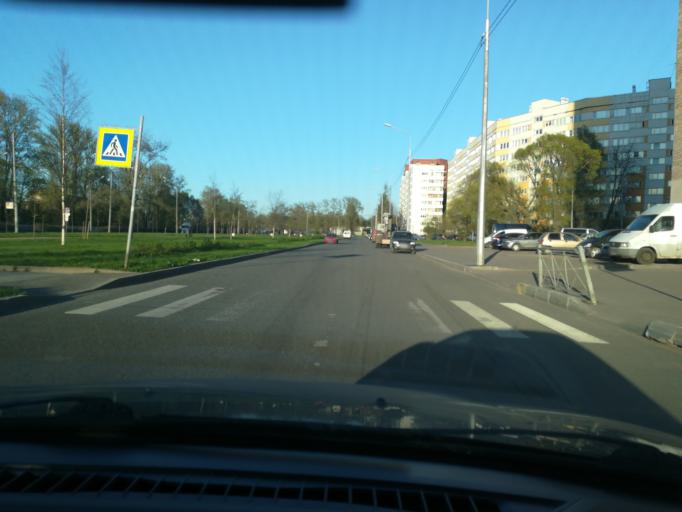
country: RU
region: St.-Petersburg
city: Avtovo
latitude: 59.8627
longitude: 30.2492
